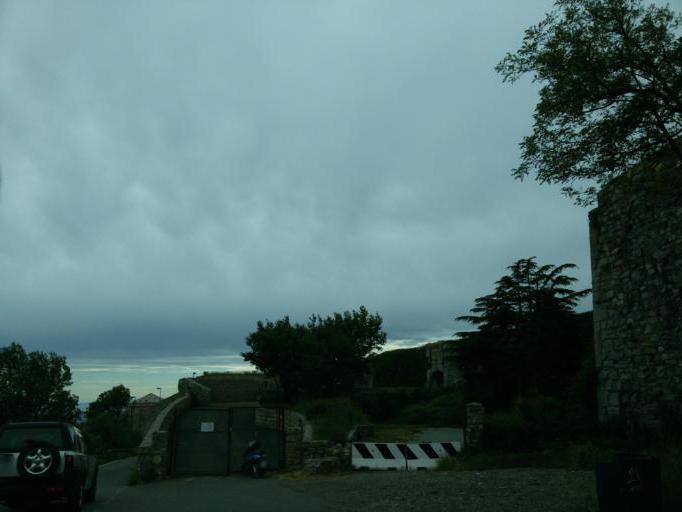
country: IT
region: Liguria
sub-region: Provincia di Genova
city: Genoa
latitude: 44.4376
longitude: 8.9207
